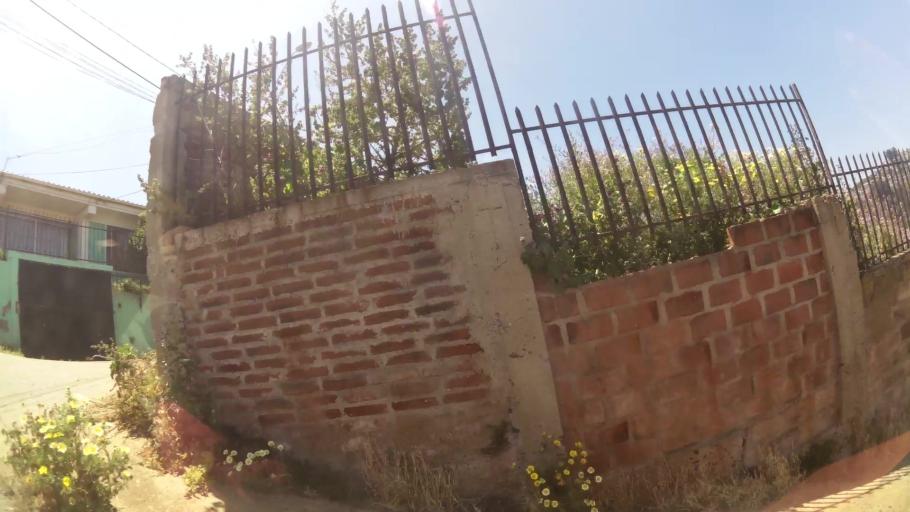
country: CL
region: Valparaiso
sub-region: Provincia de Valparaiso
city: Valparaiso
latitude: -33.0308
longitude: -71.6487
